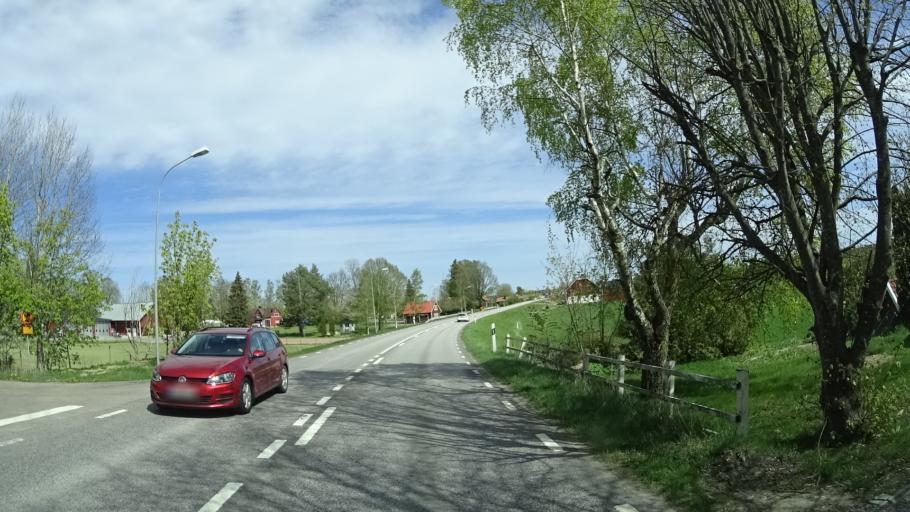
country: SE
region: OEstergoetland
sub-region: Mjolby Kommun
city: Mantorp
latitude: 58.3658
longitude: 15.3107
